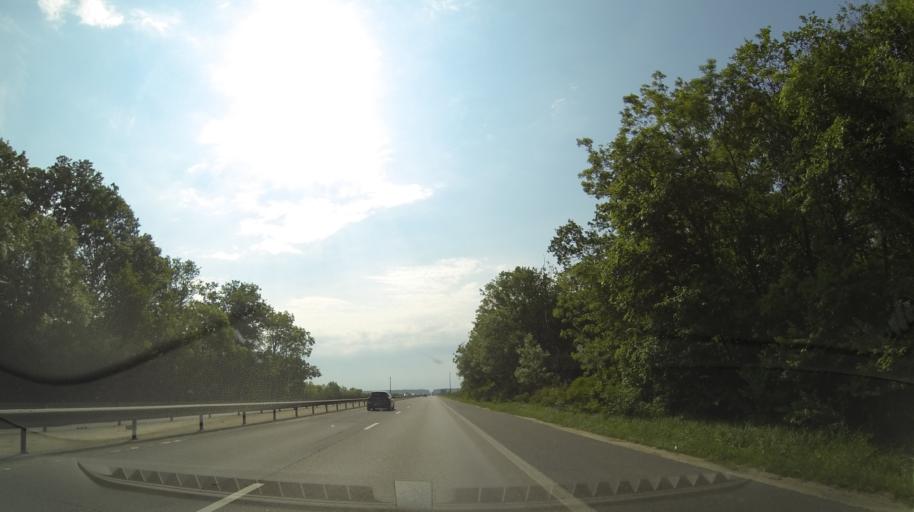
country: RO
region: Giurgiu
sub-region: Comuna Vanatorii Mici
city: Vanatorii Mari
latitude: 44.5248
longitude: 25.5444
